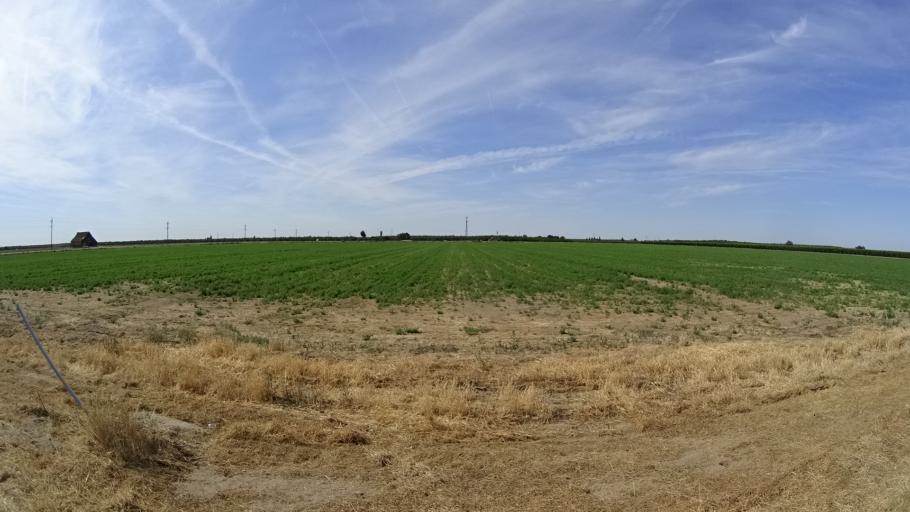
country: US
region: California
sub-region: Kings County
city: Lucerne
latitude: 36.4157
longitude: -119.6389
